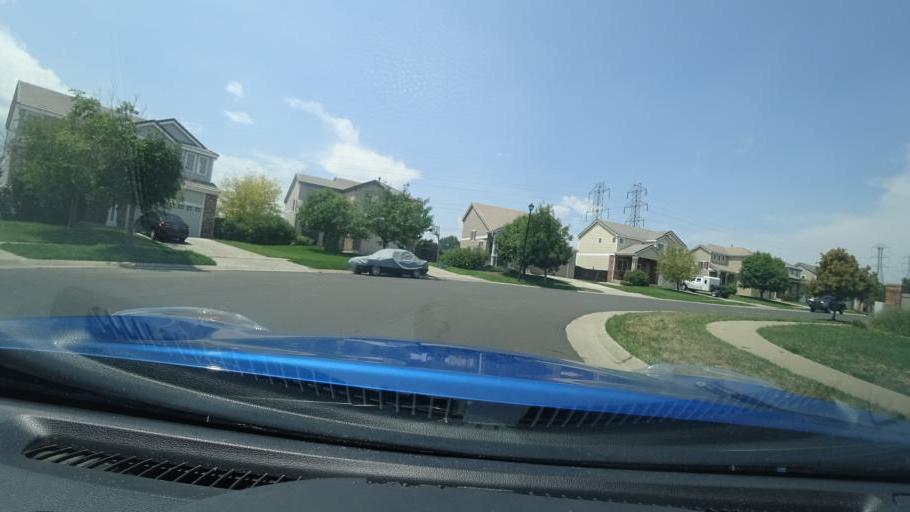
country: US
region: Colorado
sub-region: Adams County
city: Aurora
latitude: 39.6710
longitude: -104.7709
